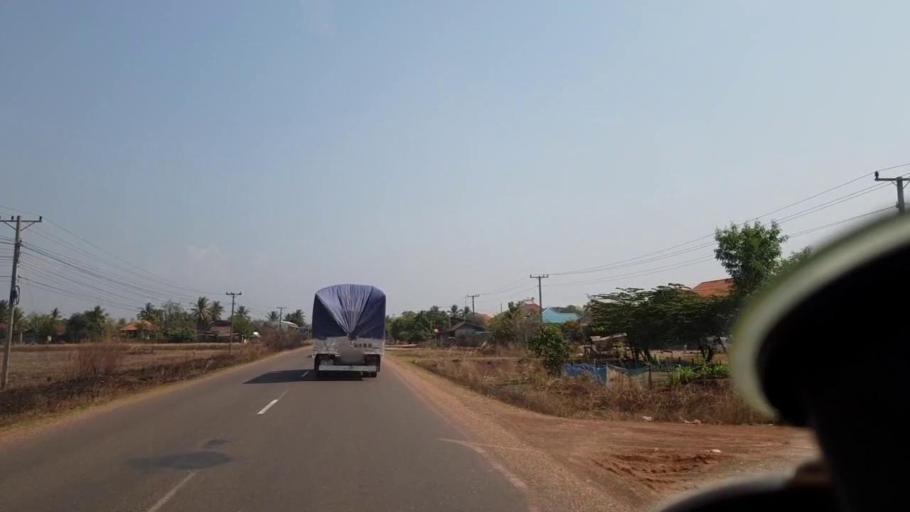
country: TH
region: Nong Khai
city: Phon Phisai
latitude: 18.0730
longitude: 102.9097
